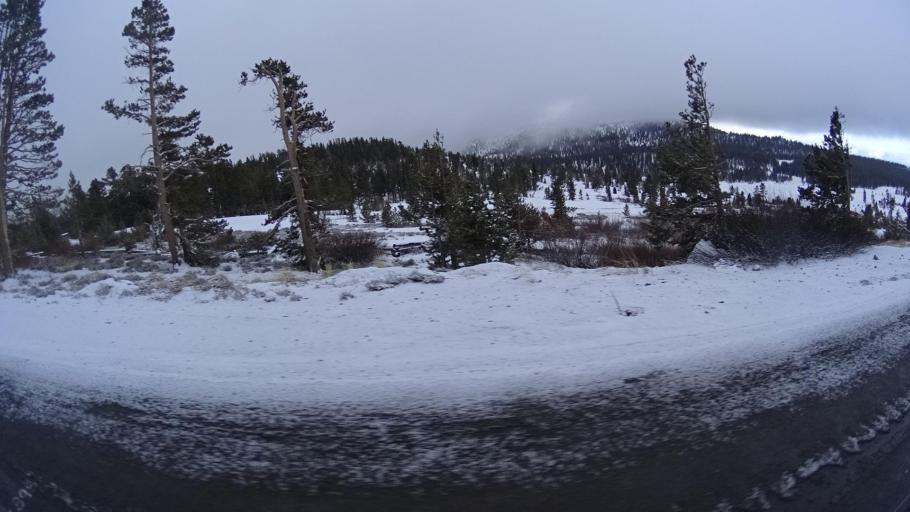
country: US
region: Nevada
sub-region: Washoe County
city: Incline Village
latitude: 39.3076
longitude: -119.9092
